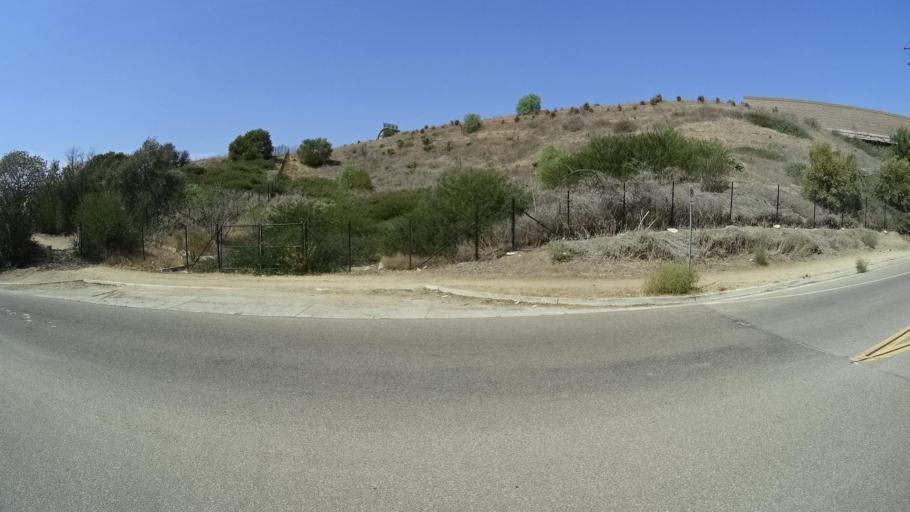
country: US
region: California
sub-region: San Diego County
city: La Presa
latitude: 32.6804
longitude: -116.9985
